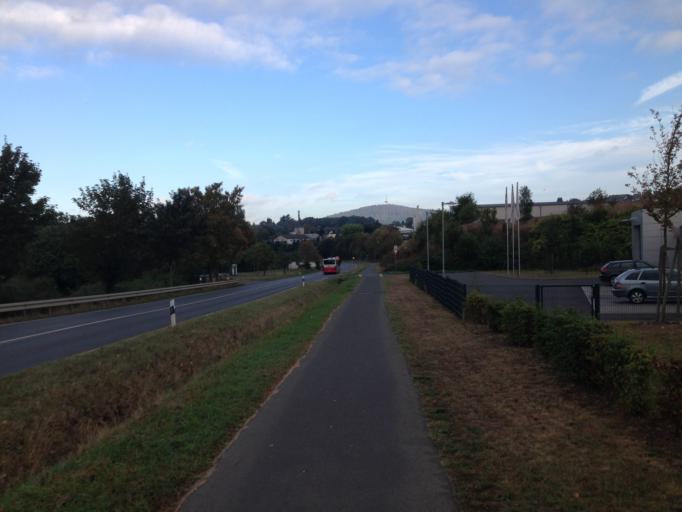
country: DE
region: Hesse
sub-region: Regierungsbezirk Giessen
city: Heuchelheim
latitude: 50.6103
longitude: 8.6141
